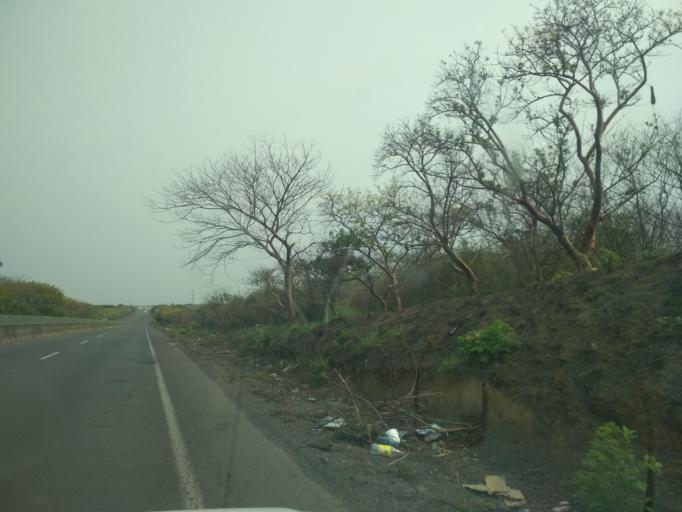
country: MX
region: Veracruz
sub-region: Veracruz
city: Las Amapolas
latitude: 19.1278
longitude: -96.2444
